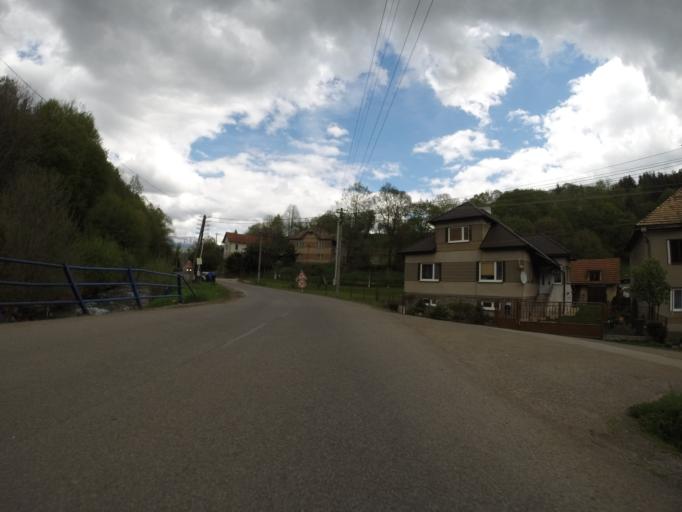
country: SK
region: Banskobystricky
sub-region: Okres Banska Bystrica
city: Brezno
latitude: 48.8306
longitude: 19.5045
